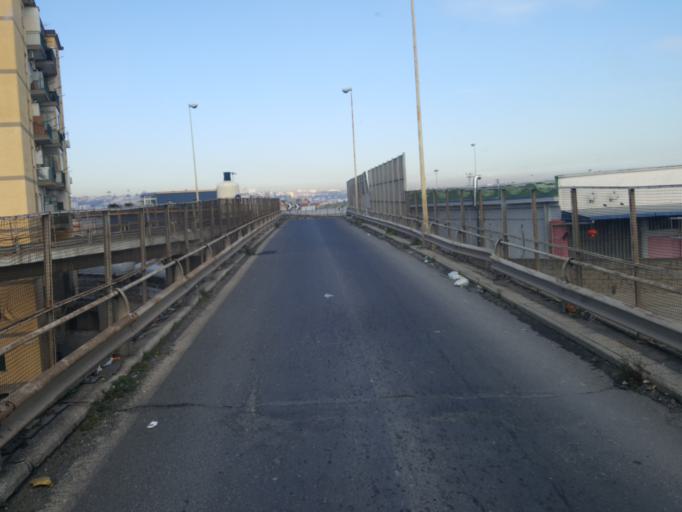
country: IT
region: Campania
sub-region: Provincia di Napoli
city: San Giorgio a Cremano
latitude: 40.8464
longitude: 14.3044
